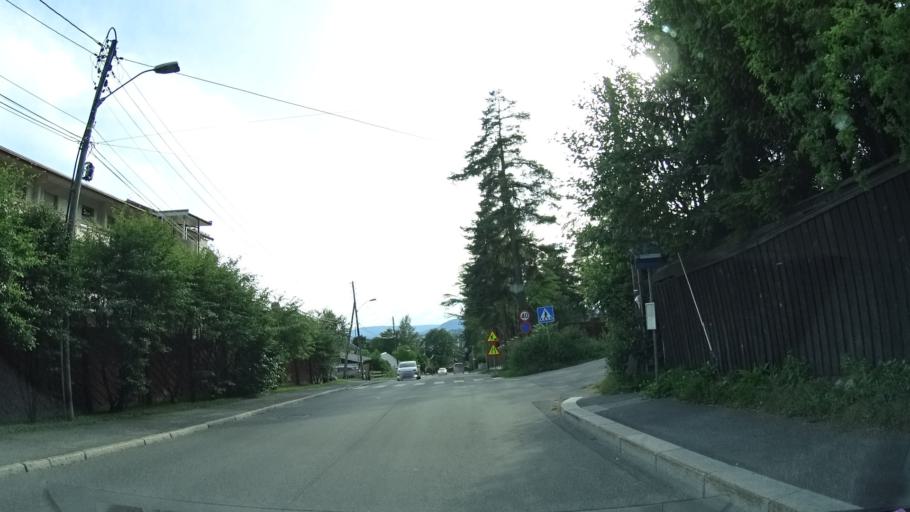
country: NO
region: Oslo
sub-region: Oslo
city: Sjolyststranda
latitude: 59.9562
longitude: 10.6620
